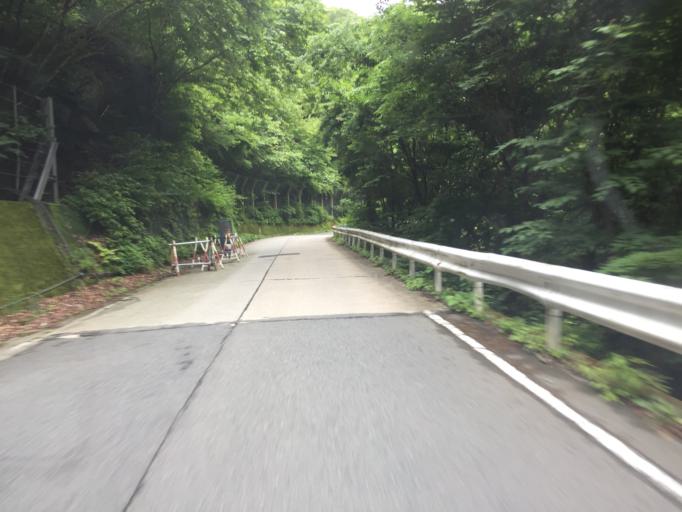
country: JP
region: Fukushima
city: Namie
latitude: 37.6864
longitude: 140.8737
